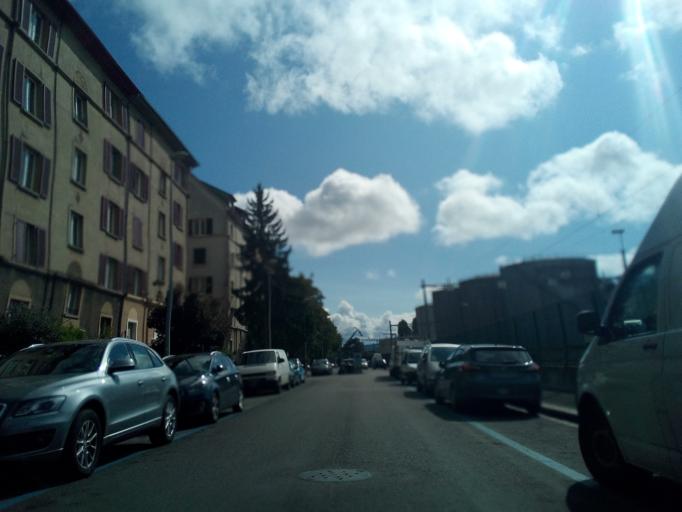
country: FR
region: Alsace
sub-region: Departement du Haut-Rhin
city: Village-Neuf
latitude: 47.5775
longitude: 7.5880
